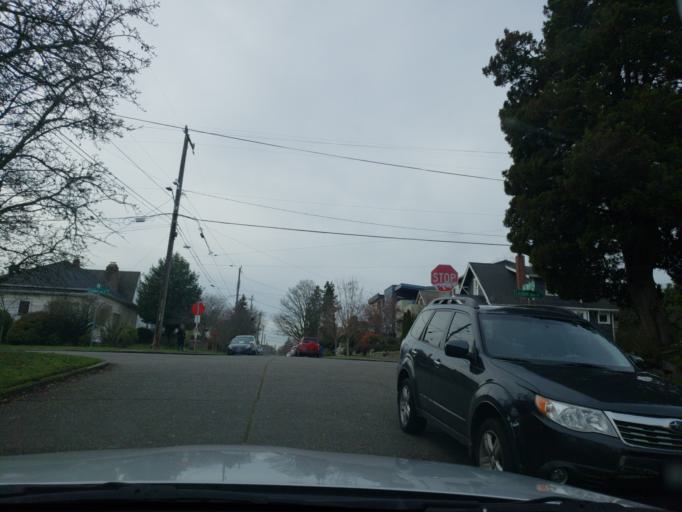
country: US
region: Washington
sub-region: King County
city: Shoreline
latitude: 47.6877
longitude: -122.3469
